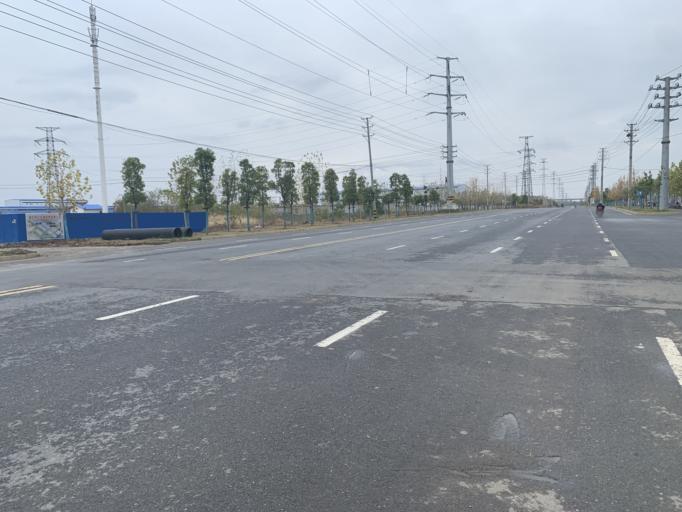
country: CN
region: Hubei
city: Nancheng
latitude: 31.2237
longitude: 113.6801
